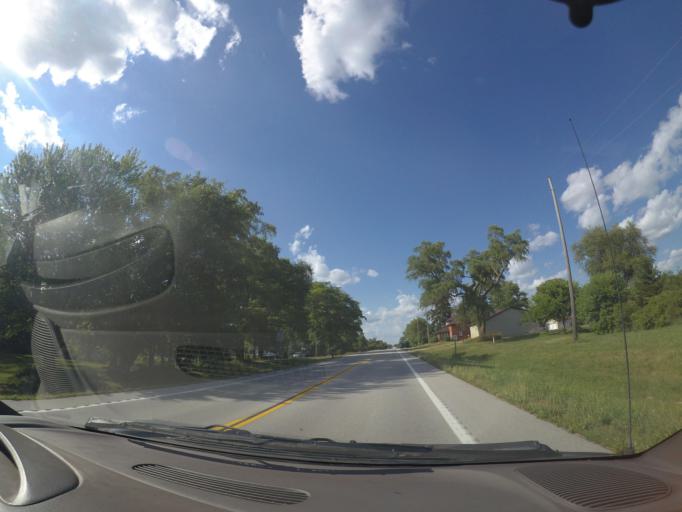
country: US
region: Ohio
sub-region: Wood County
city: Pemberville
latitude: 41.4127
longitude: -83.4158
